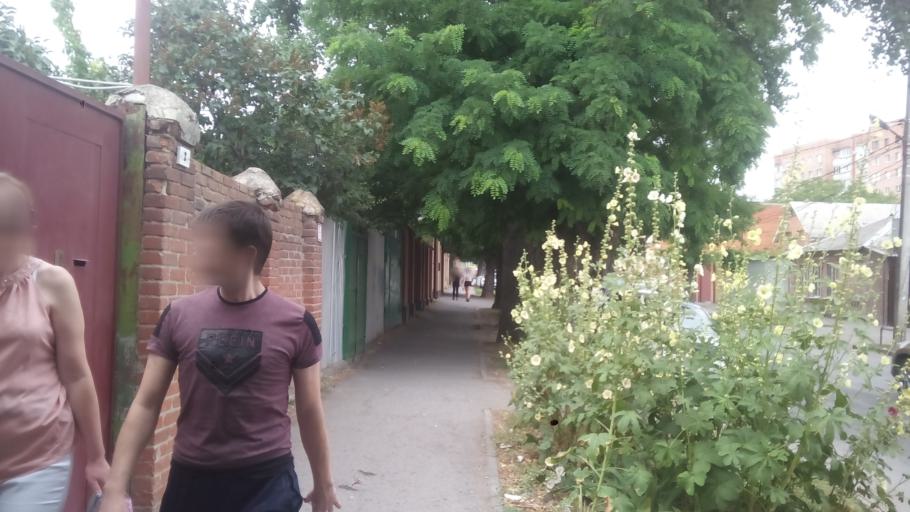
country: RU
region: Rostov
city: Rostov-na-Donu
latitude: 47.2128
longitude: 39.6740
